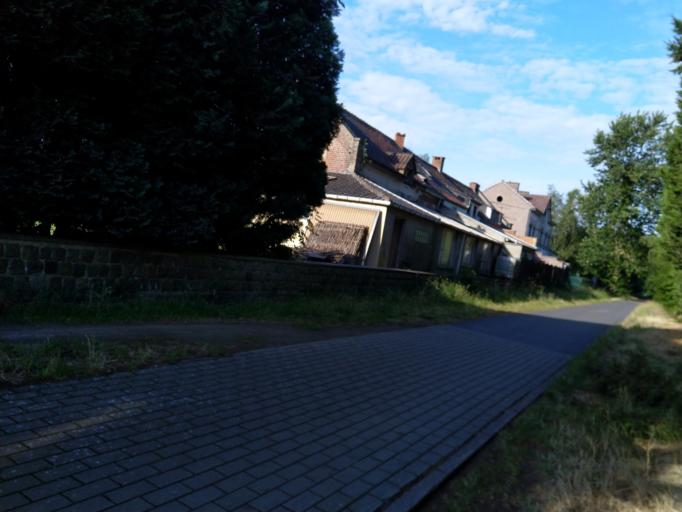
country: BE
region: Wallonia
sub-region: Province du Hainaut
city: Estinnes-au-Val
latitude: 50.3894
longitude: 4.1336
